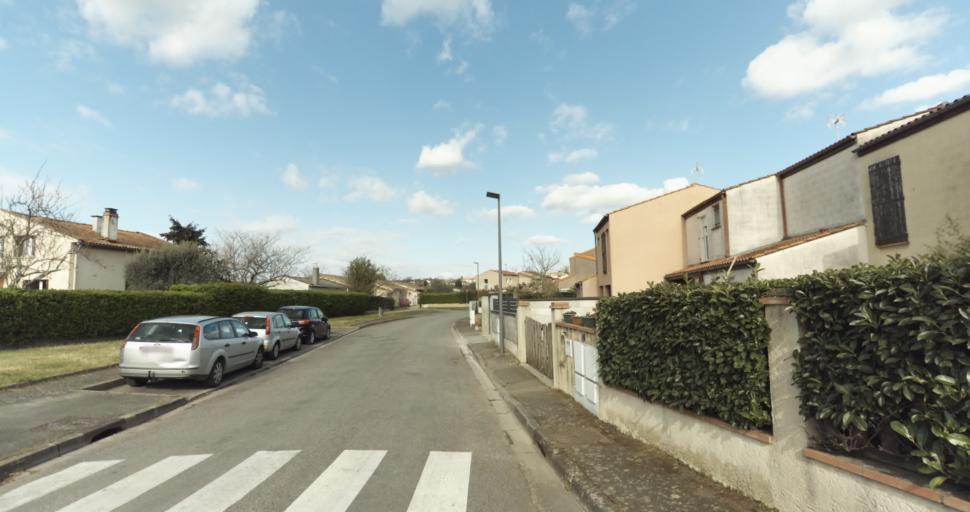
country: FR
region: Midi-Pyrenees
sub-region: Departement de la Haute-Garonne
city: Auterive
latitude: 43.3456
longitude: 1.4837
